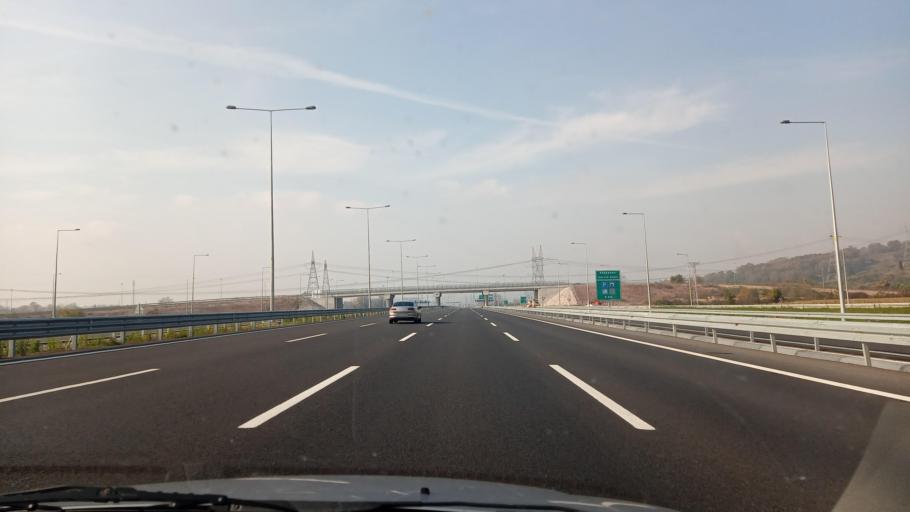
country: TR
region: Sakarya
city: Kazimpasa
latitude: 40.8416
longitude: 30.3505
